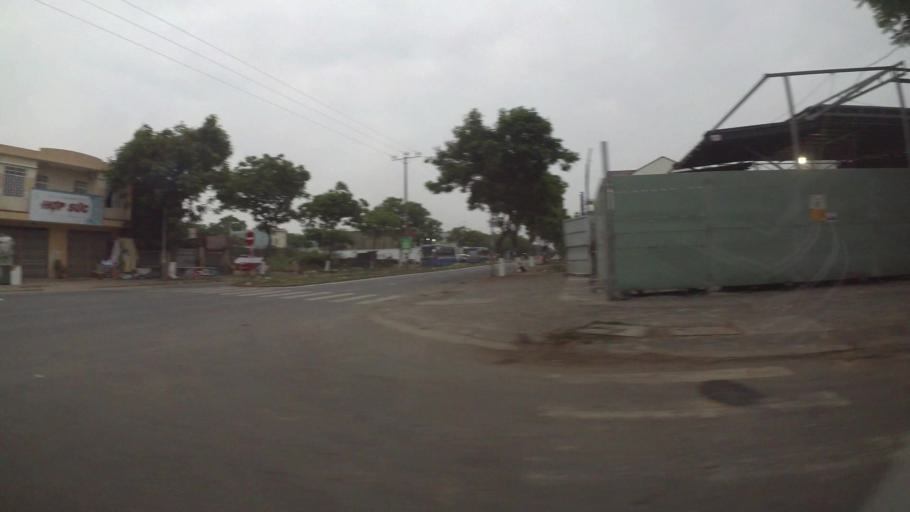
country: VN
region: Da Nang
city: Thanh Khe
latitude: 16.0513
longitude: 108.1738
